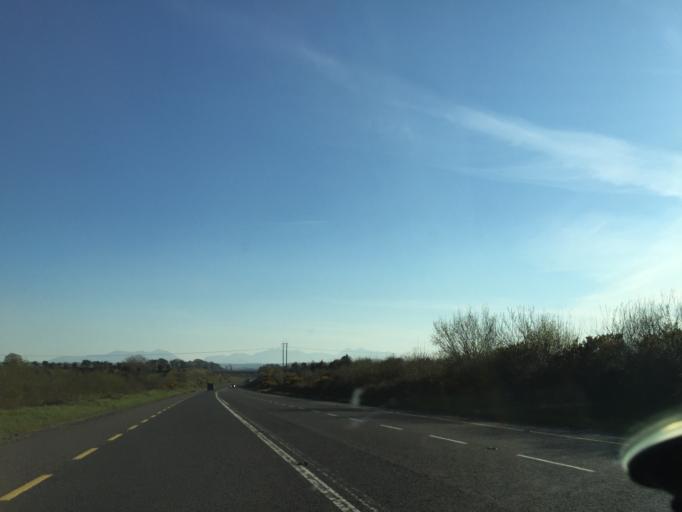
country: IE
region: Munster
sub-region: Ciarrai
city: Castleisland
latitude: 52.2093
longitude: -9.5665
